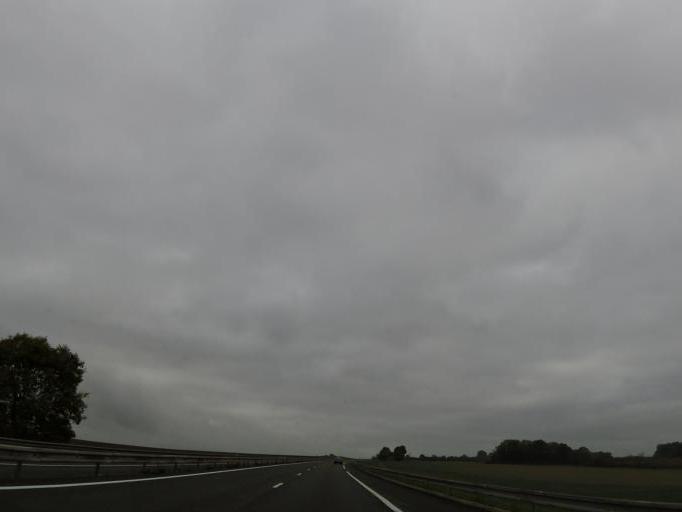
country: FR
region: Ile-de-France
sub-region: Departement de Seine-et-Marne
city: Sammeron
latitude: 48.9799
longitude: 3.0757
